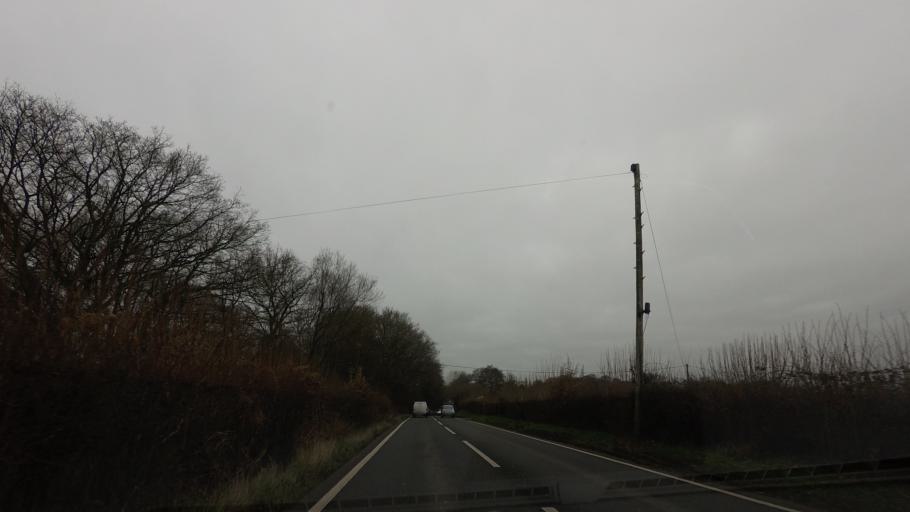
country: GB
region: England
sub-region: East Sussex
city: Saint Leonards-on-Sea
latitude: 50.9053
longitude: 0.5494
